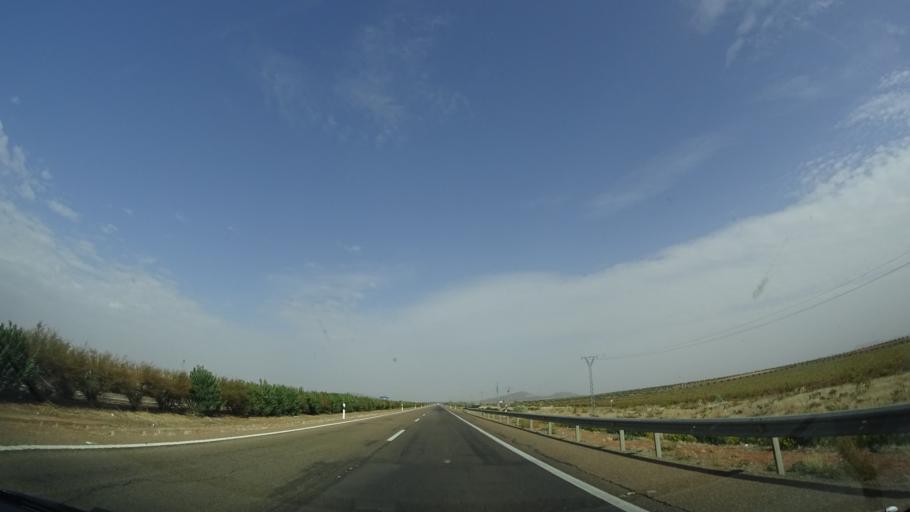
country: ES
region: Extremadura
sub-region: Provincia de Badajoz
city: Almendralejo
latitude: 38.7305
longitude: -6.3924
